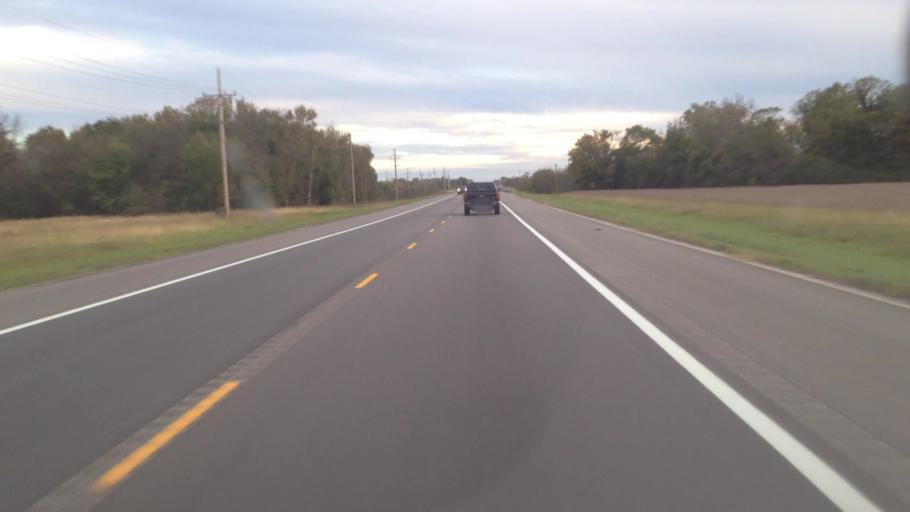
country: US
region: Kansas
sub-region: Franklin County
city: Ottawa
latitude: 38.5569
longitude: -95.2679
